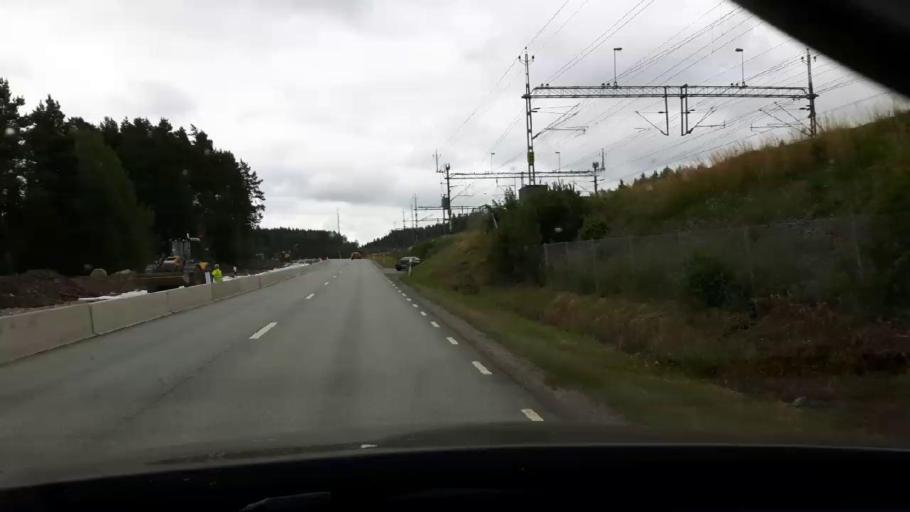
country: SE
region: Stockholm
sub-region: Sigtuna Kommun
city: Rosersberg
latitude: 59.5510
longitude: 17.8961
